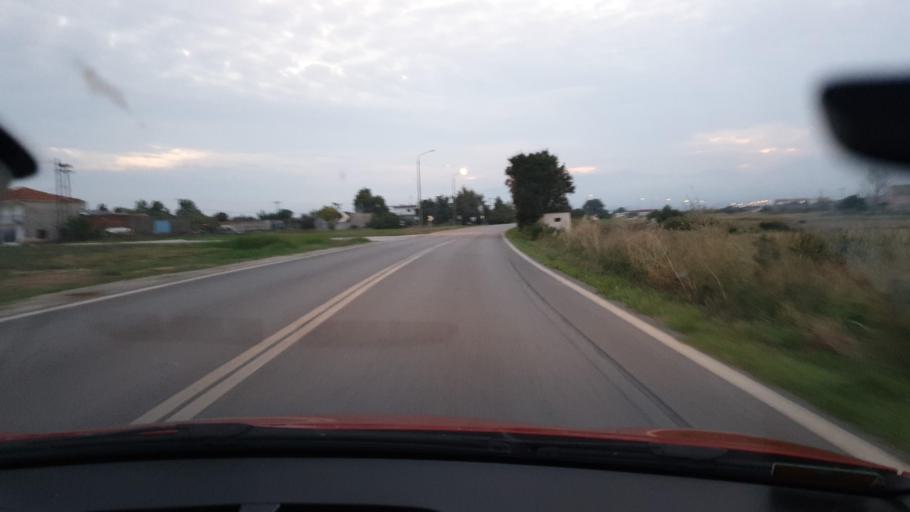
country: GR
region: Central Macedonia
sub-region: Nomos Kilkis
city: Polykastro
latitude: 40.9904
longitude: 22.6179
